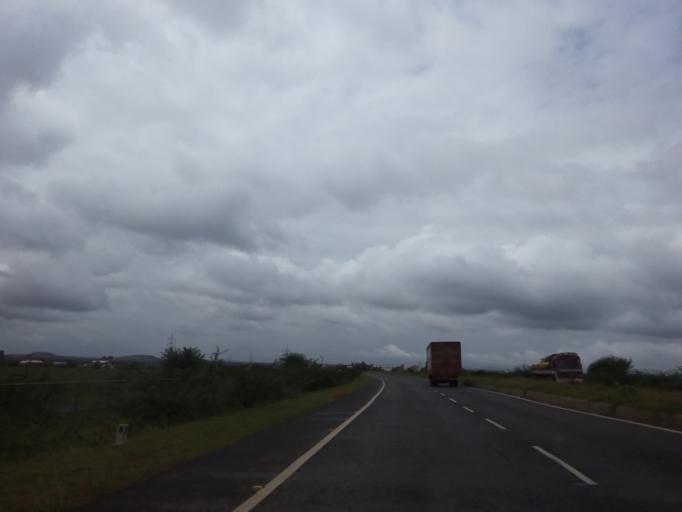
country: IN
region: Karnataka
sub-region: Haveri
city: Haveri
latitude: 14.7901
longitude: 75.3811
